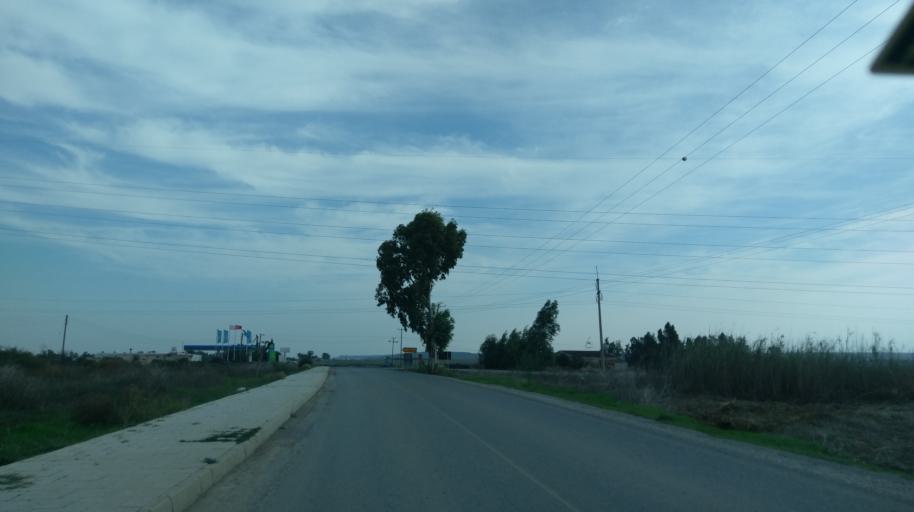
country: CY
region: Lefkosia
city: Mammari
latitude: 35.2264
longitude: 33.1721
